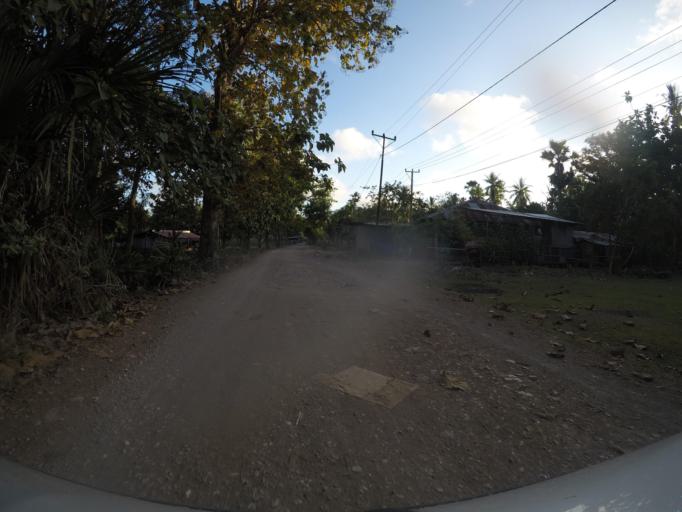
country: TL
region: Baucau
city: Venilale
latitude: -8.7447
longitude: 126.7137
